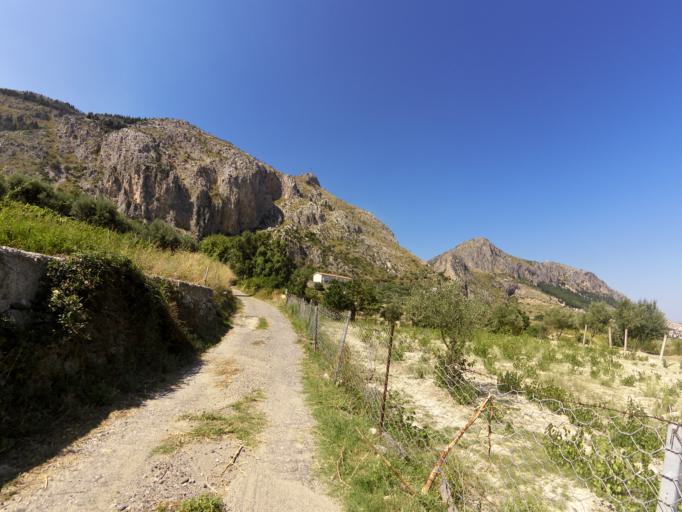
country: IT
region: Calabria
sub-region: Provincia di Reggio Calabria
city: Pazzano
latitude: 38.4643
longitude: 16.4544
